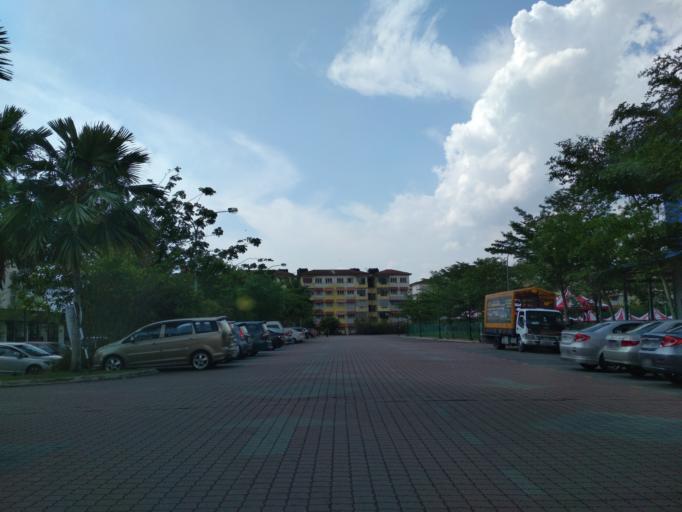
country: MY
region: Perak
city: Kampar
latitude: 4.3284
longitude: 101.1451
